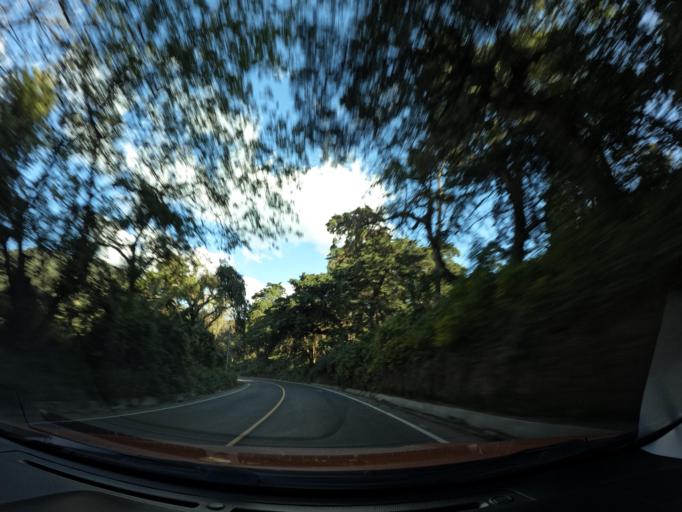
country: GT
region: Sacatepequez
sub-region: Municipio de Santa Maria de Jesus
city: Santa Maria de Jesus
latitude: 14.4773
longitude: -90.6971
